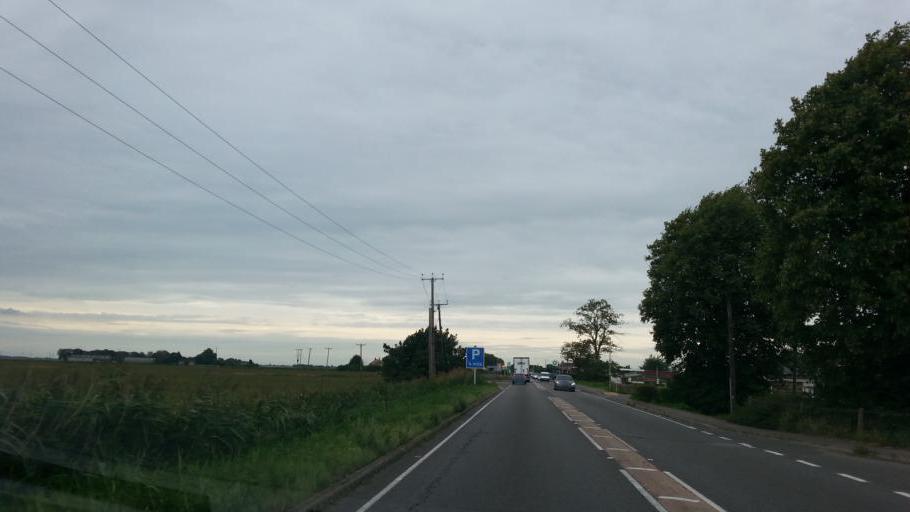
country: GB
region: England
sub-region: Peterborough
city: Thorney
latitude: 52.6162
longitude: -0.0145
